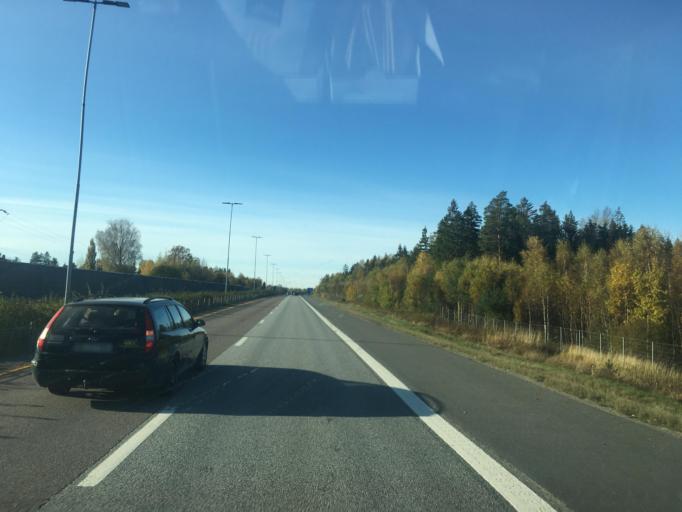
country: NO
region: Ostfold
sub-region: Rade
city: Karlshus
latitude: 59.3555
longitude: 10.8683
